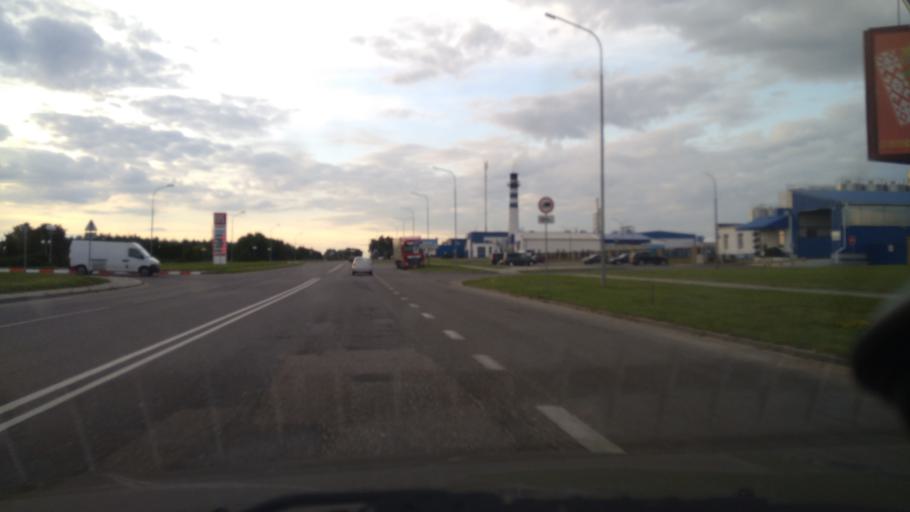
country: BY
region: Grodnenskaya
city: Shchuchin
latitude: 53.5894
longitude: 24.7457
